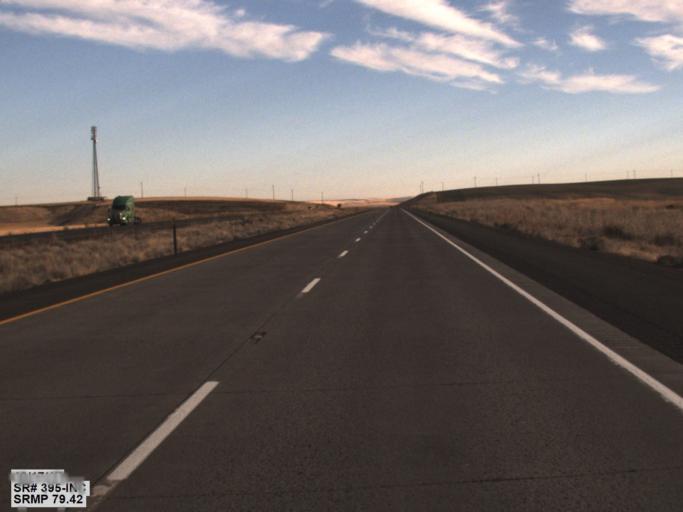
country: US
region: Washington
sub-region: Adams County
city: Ritzville
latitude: 46.9331
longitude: -118.5891
